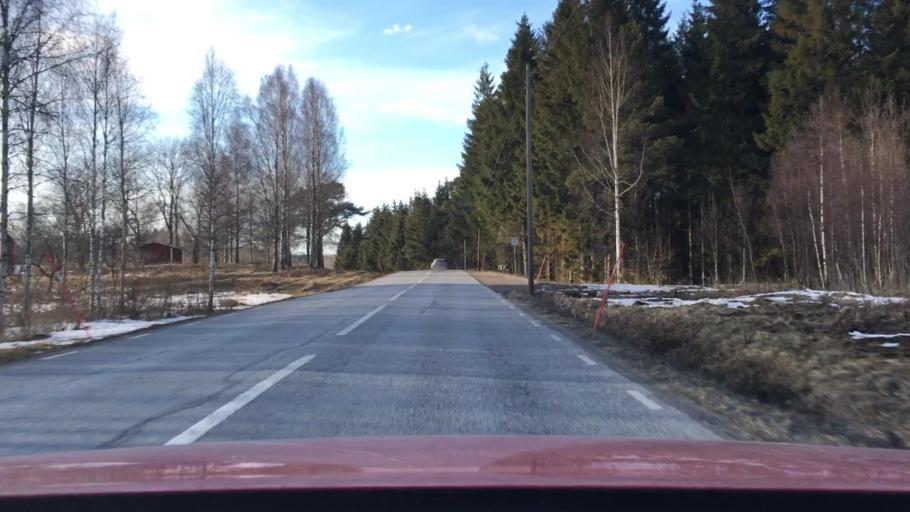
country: SE
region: Vaestra Goetaland
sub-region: Tanums Kommun
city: Tanumshede
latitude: 58.8102
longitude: 11.5503
